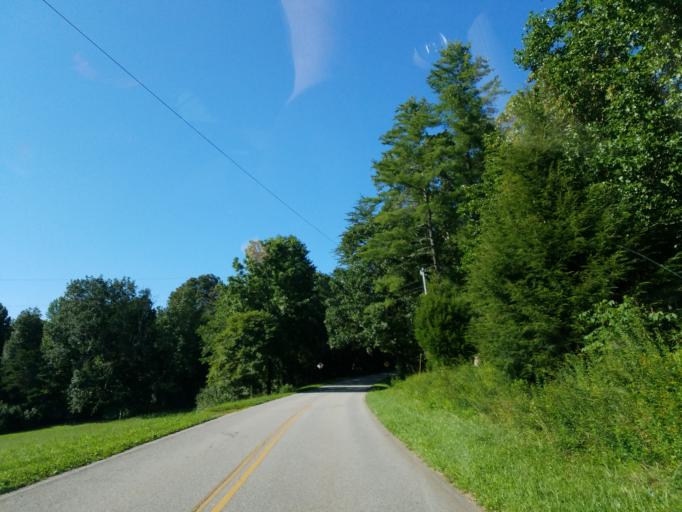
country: US
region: Georgia
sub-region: Fannin County
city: Blue Ridge
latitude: 34.7488
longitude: -84.2262
